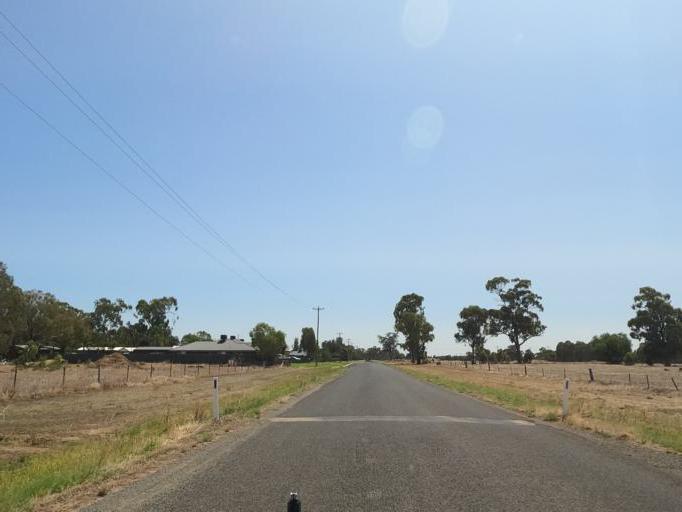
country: AU
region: New South Wales
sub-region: Corowa Shire
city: Mulwala
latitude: -35.9838
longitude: 146.0003
